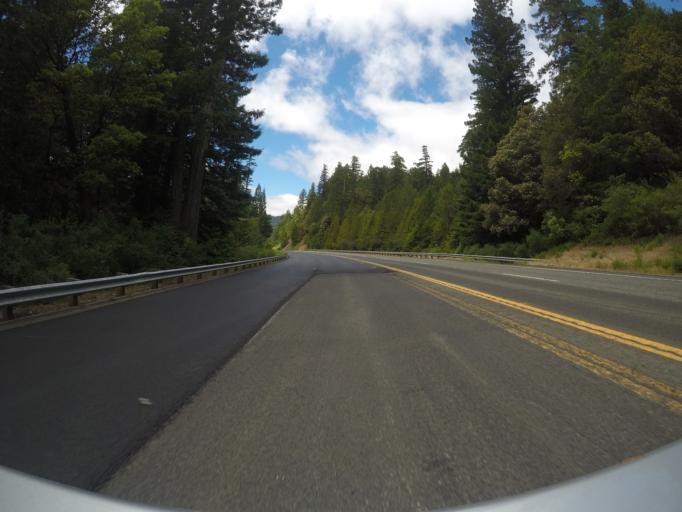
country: US
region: California
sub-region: Humboldt County
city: Redway
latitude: 40.2846
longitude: -123.8890
